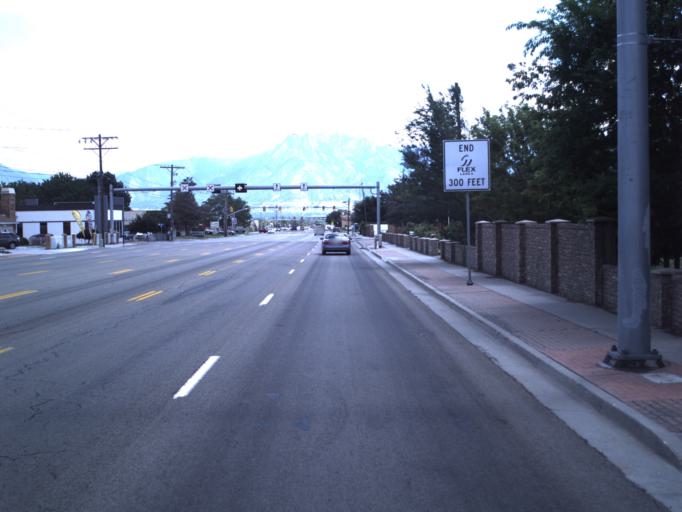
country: US
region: Utah
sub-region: Salt Lake County
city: Taylorsville
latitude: 40.6530
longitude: -111.9458
